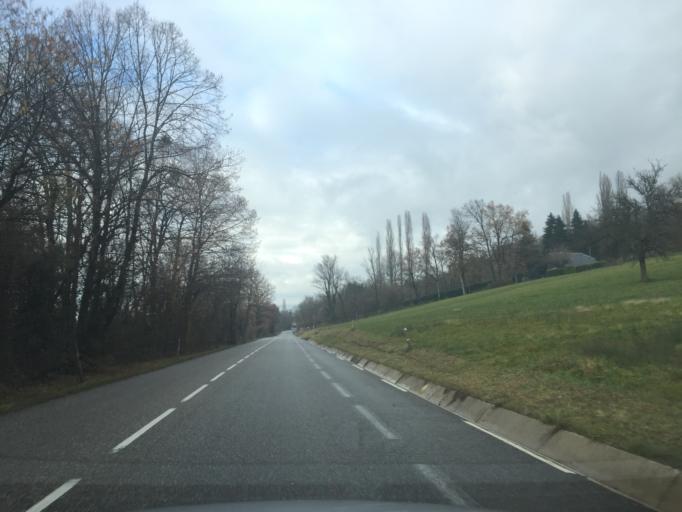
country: FR
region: Rhone-Alpes
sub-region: Departement de la Savoie
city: Mouxy
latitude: 45.6886
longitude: 5.9391
